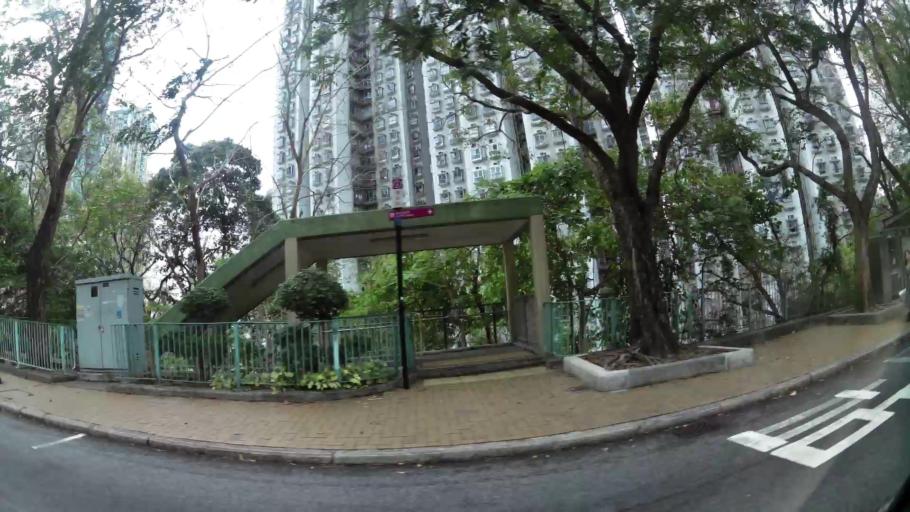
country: HK
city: Hong Kong
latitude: 22.2819
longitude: 114.1322
